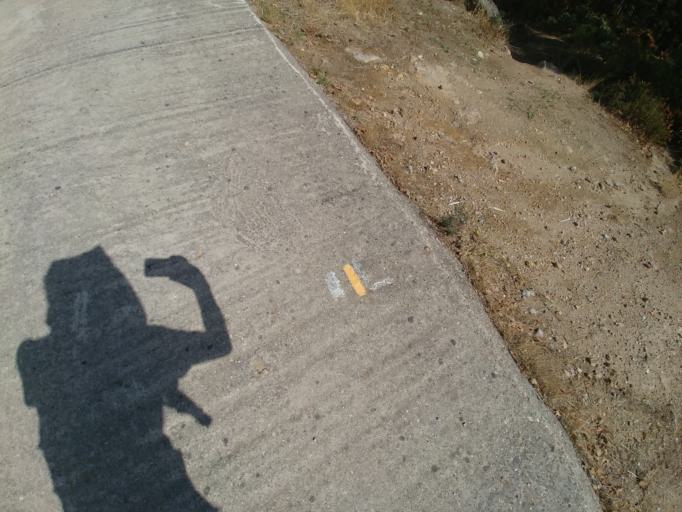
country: ES
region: Extremadura
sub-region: Provincia de Caceres
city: Garganta la Olla
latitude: 40.1118
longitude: -5.7450
